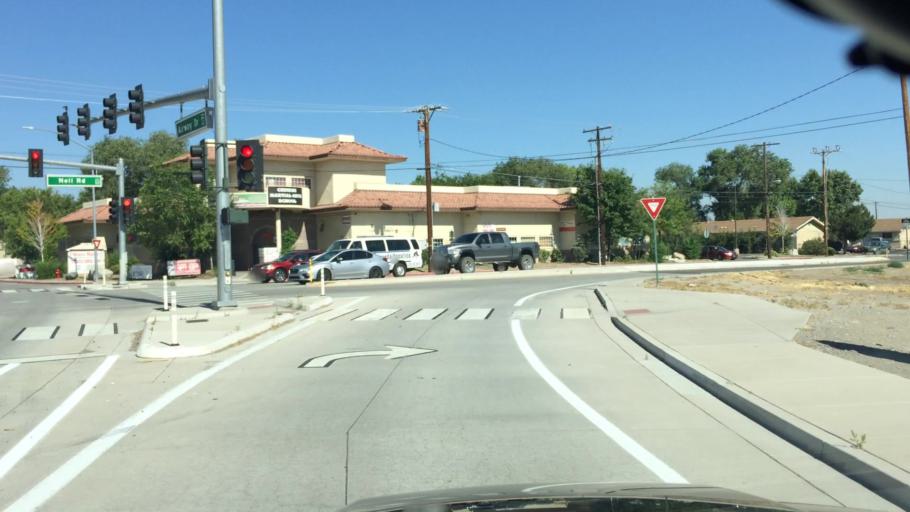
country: US
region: Nevada
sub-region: Washoe County
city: Reno
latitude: 39.4929
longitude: -119.7801
